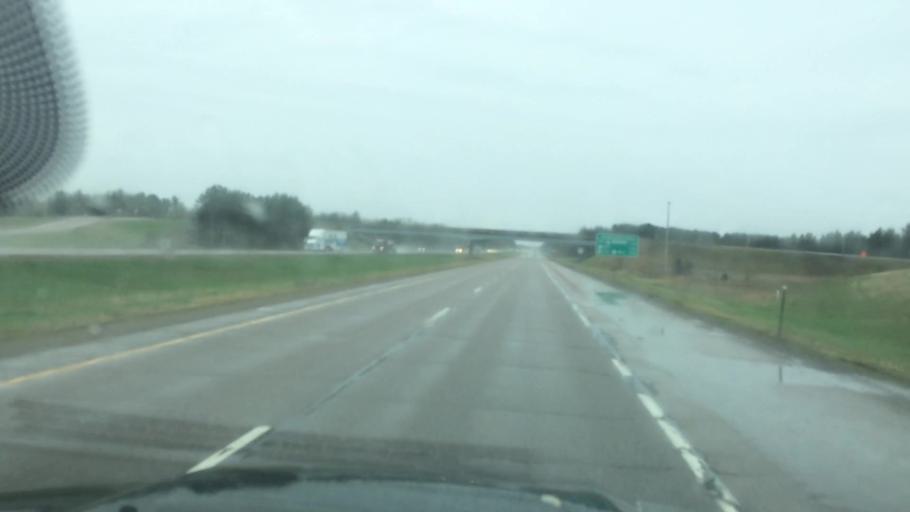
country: US
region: Wisconsin
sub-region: Portage County
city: Stevens Point
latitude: 44.5720
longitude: -89.6002
